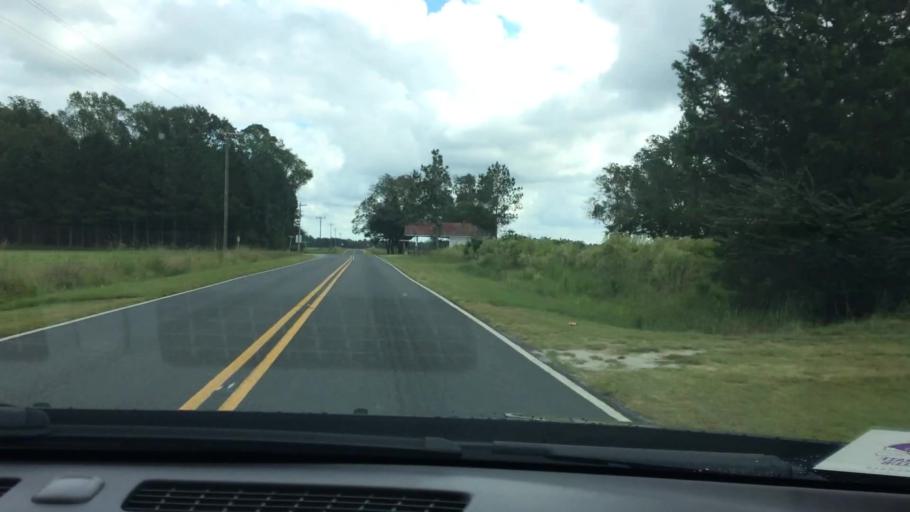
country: US
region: North Carolina
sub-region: Greene County
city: Maury
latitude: 35.5190
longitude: -77.5318
